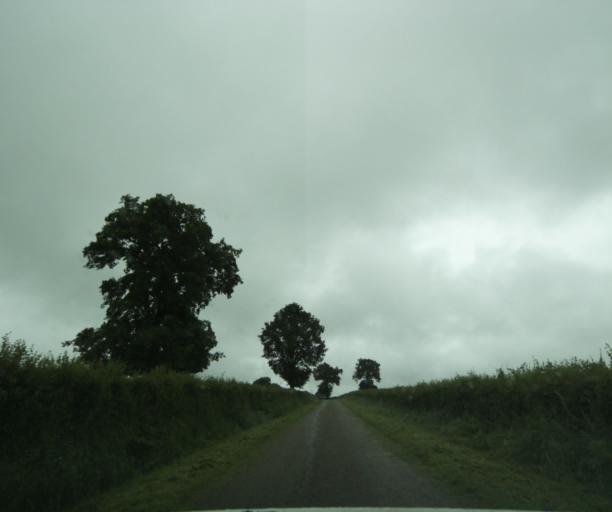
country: FR
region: Bourgogne
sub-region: Departement de Saone-et-Loire
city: Charolles
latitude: 46.4283
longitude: 4.3245
